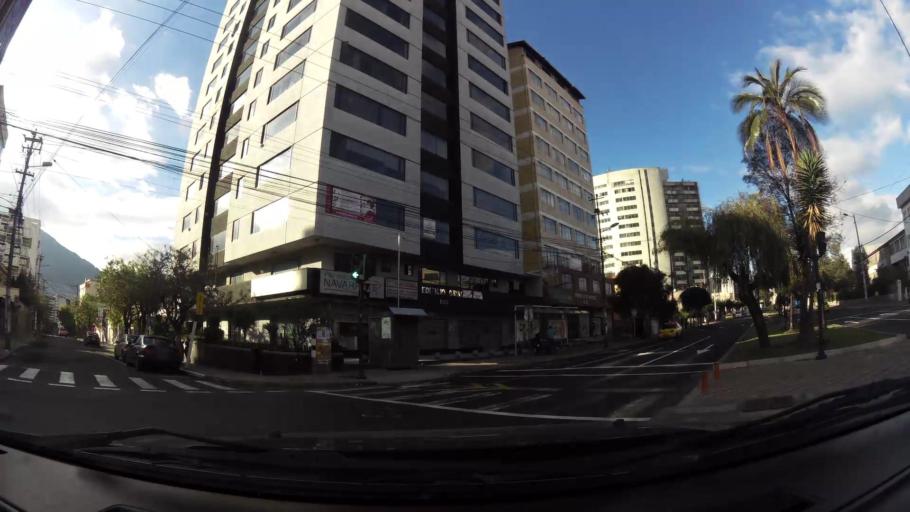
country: EC
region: Pichincha
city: Quito
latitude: -0.2089
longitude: -78.4917
